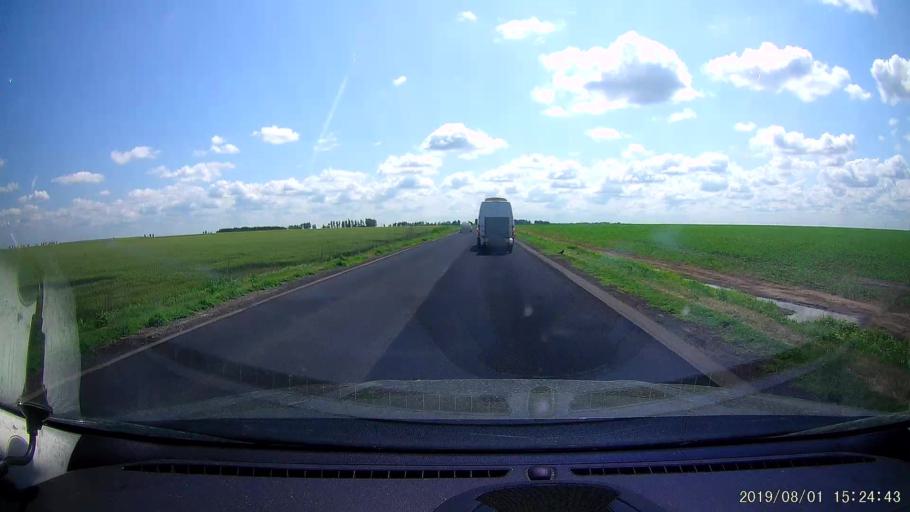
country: RO
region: Braila
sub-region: Comuna Viziru
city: Lanurile
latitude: 45.0305
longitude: 27.7459
